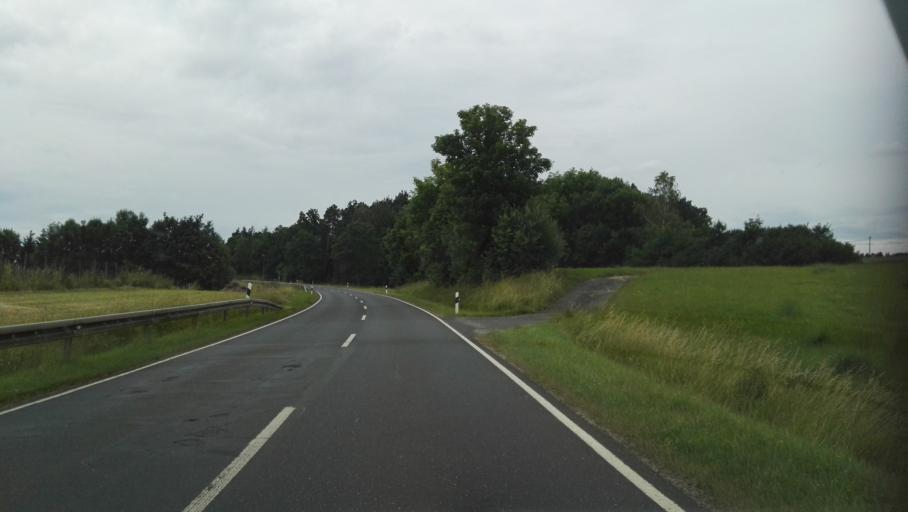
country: DE
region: Bavaria
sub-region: Upper Franconia
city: Plankenfels
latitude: 49.8978
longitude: 11.3327
